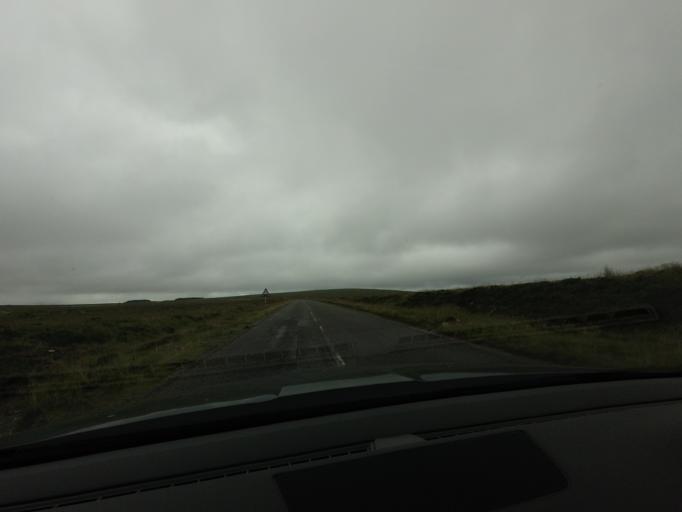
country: GB
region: Scotland
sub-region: Highland
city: Golspie
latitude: 58.5044
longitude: -4.5457
